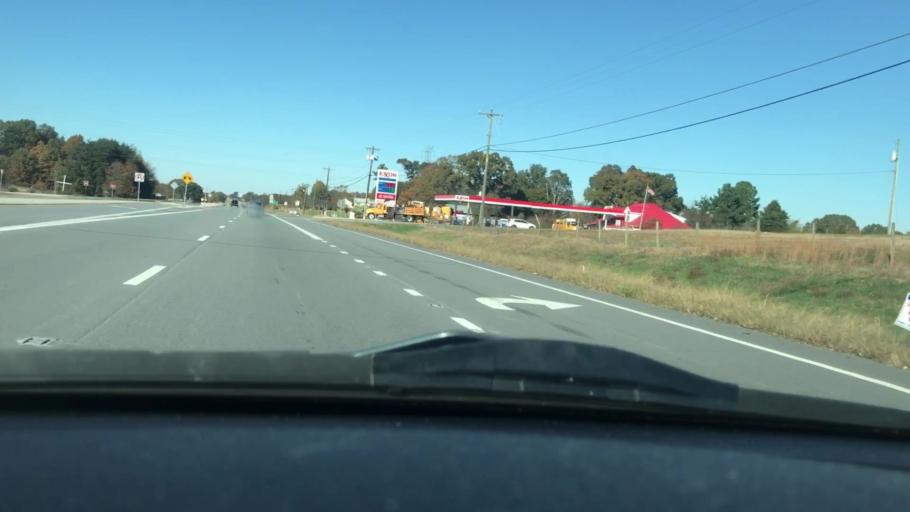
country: US
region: North Carolina
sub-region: Guilford County
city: Stokesdale
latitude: 36.2934
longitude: -79.9400
